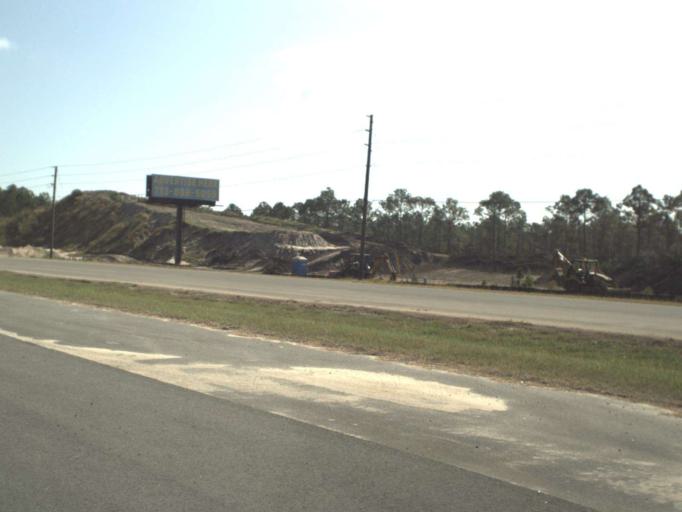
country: US
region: Florida
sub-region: Walton County
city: Freeport
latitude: 30.4453
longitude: -86.1368
